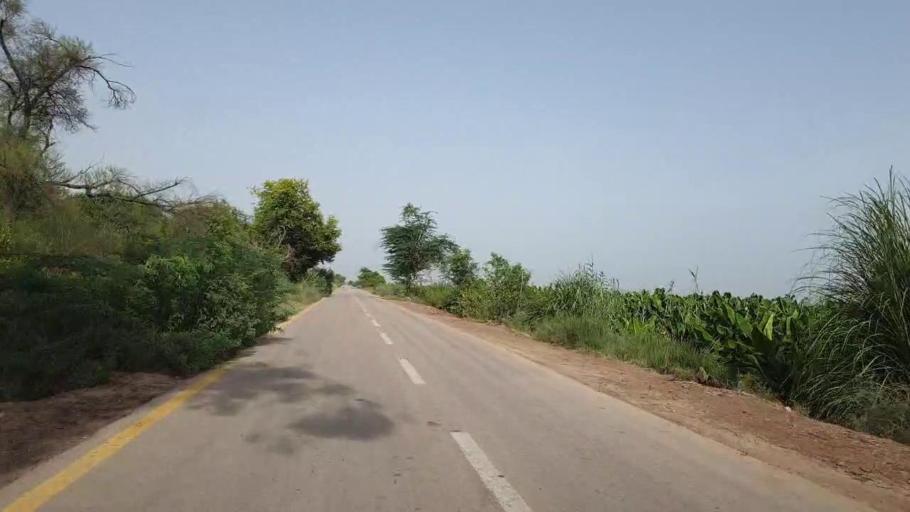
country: PK
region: Sindh
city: Bandhi
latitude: 26.5880
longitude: 68.2264
